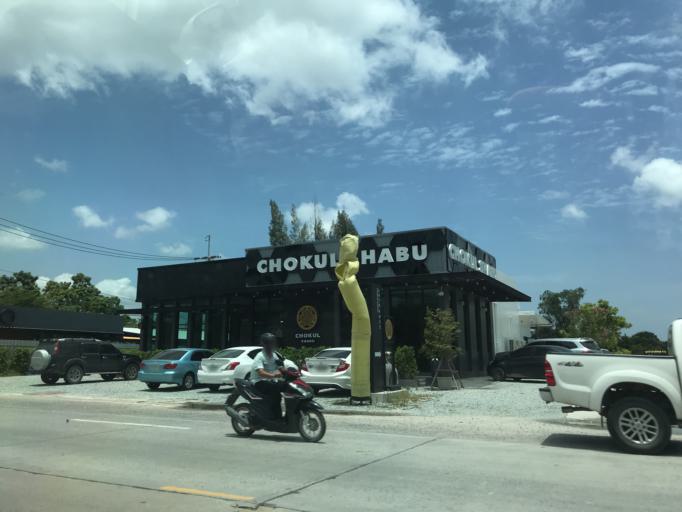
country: TH
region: Chon Buri
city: Si Racha
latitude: 13.1467
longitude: 100.9819
